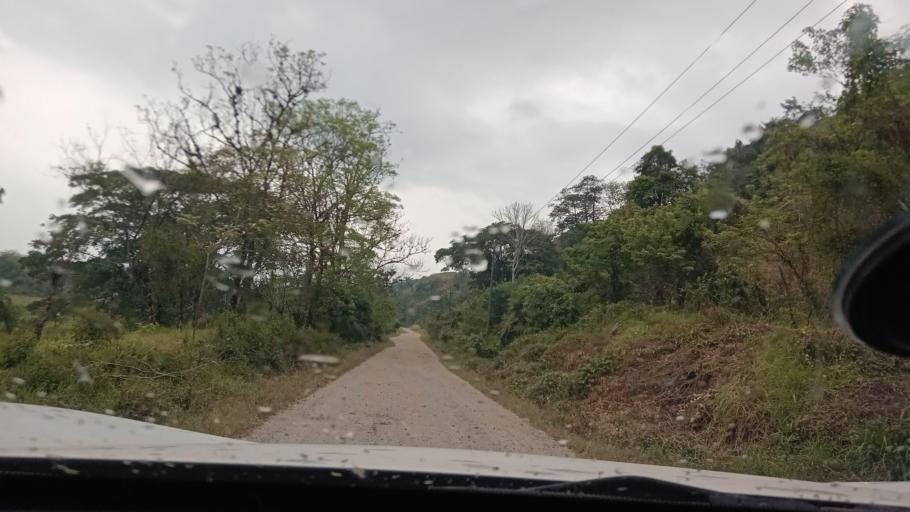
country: MX
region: Veracruz
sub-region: Uxpanapa
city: Poblado 10
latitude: 17.4509
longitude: -94.0854
